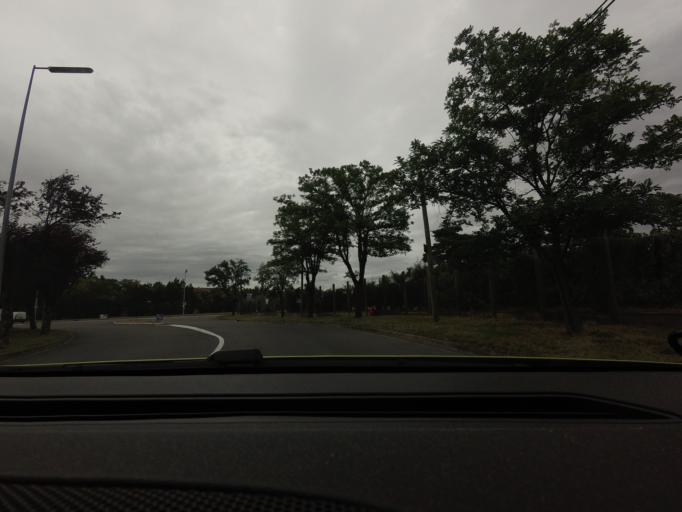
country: FR
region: Midi-Pyrenees
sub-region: Departement de la Haute-Garonne
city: Tournefeuille
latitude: 43.6036
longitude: 1.3138
